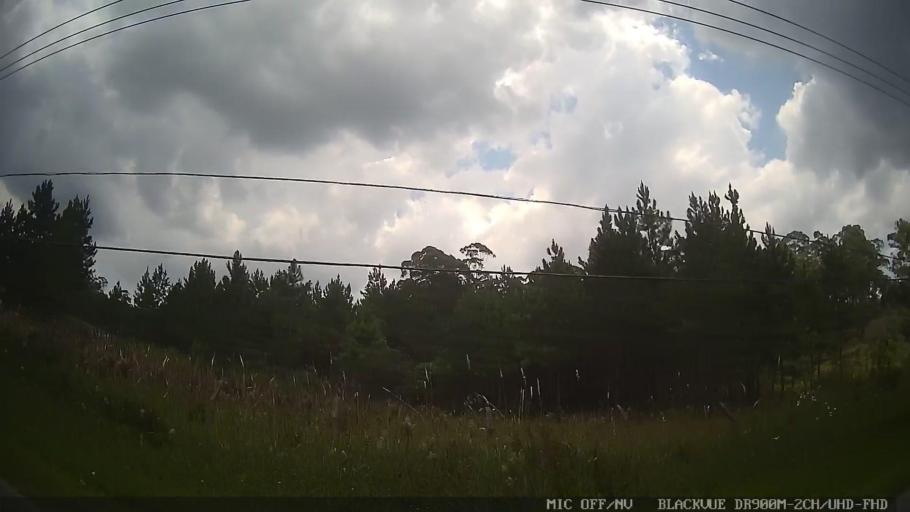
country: BR
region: Sao Paulo
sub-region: Ribeirao Pires
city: Ribeirao Pires
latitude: -23.6429
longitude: -46.3883
